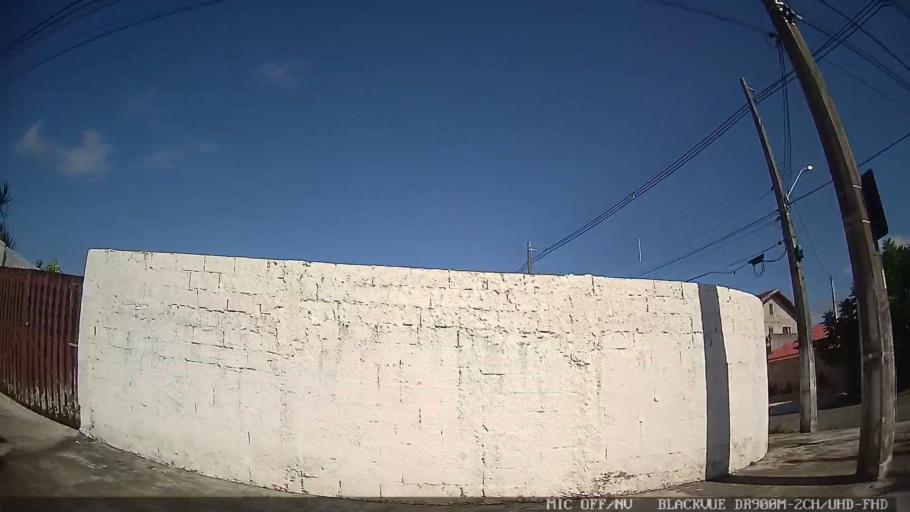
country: BR
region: Sao Paulo
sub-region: Peruibe
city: Peruibe
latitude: -24.3082
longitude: -46.9958
